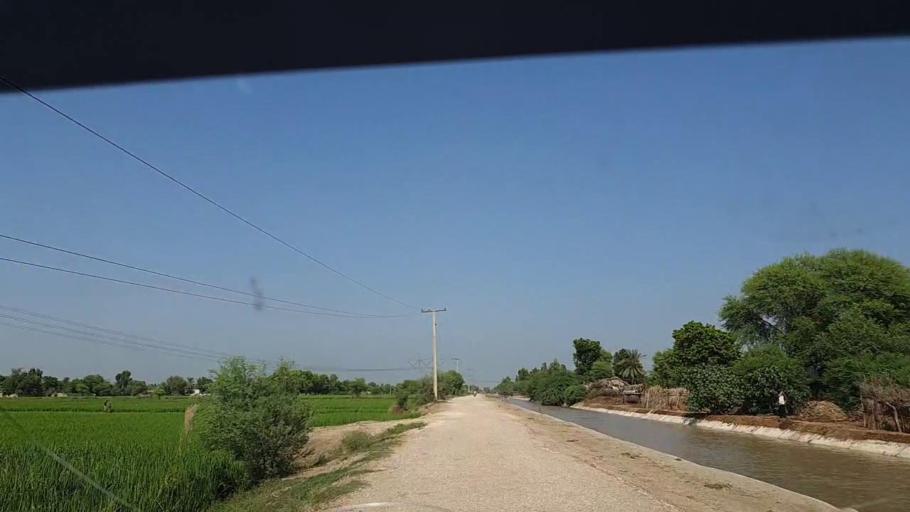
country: PK
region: Sindh
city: Ghauspur
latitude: 28.1513
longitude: 69.0806
